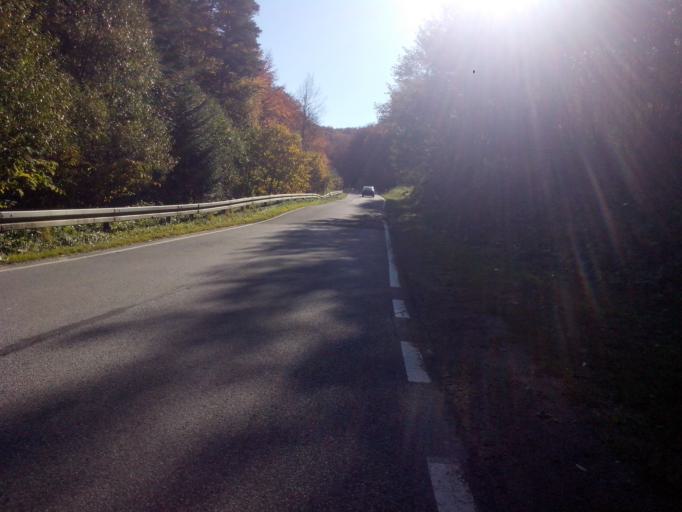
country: PL
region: Subcarpathian Voivodeship
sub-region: Powiat krosnienski
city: Korczyna
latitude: 49.7600
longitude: 21.7942
